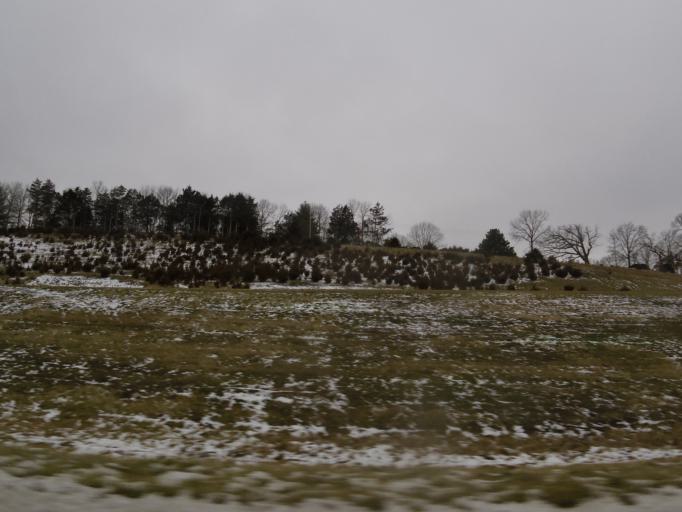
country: US
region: Missouri
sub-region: Clark County
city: Kahoka
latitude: 40.3604
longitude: -91.5872
